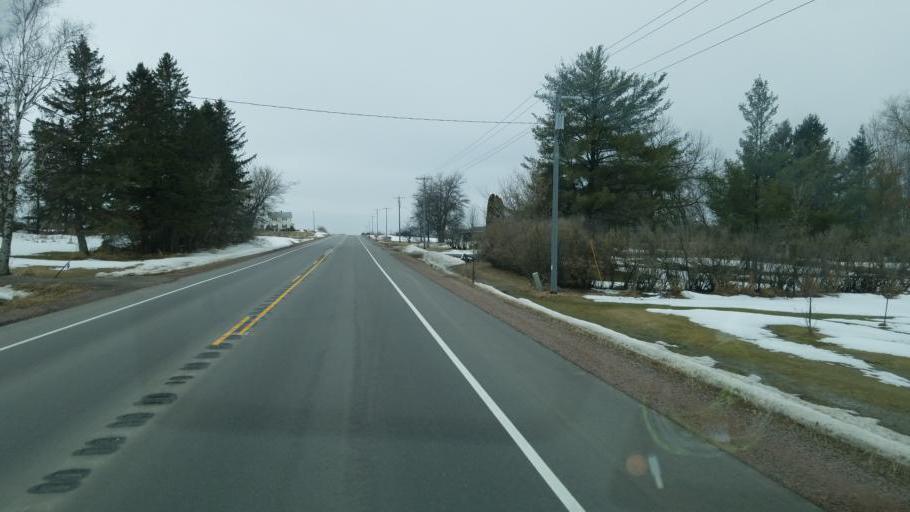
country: US
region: Wisconsin
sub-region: Wood County
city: Marshfield
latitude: 44.6559
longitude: -90.2273
